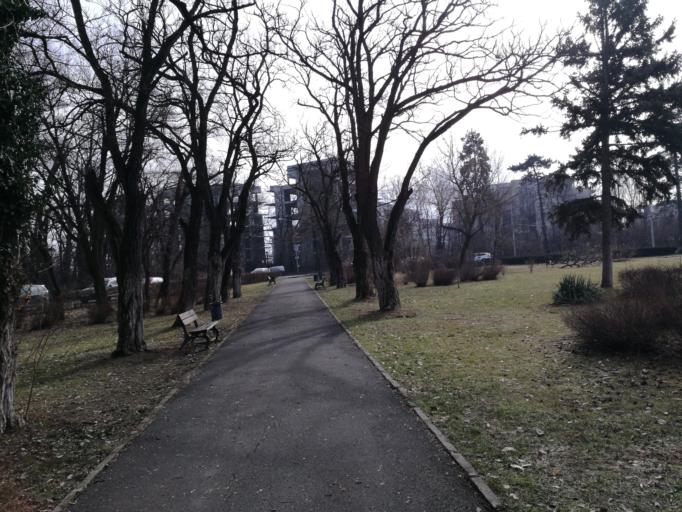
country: RO
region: Ilfov
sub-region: Comuna Otopeni
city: Otopeni
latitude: 44.5171
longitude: 26.0910
